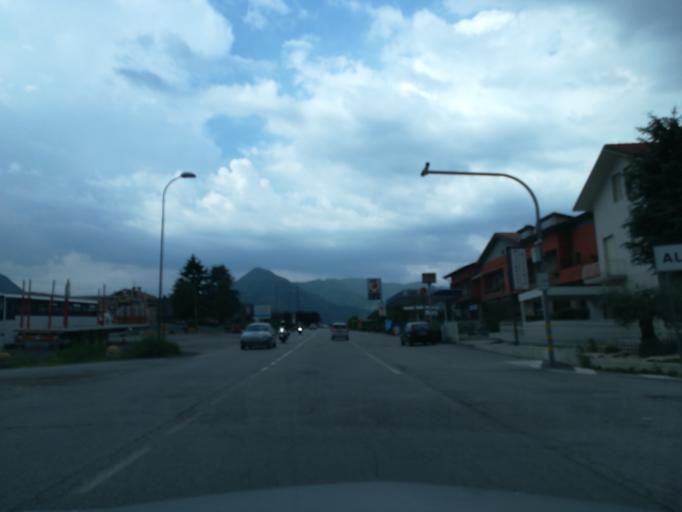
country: IT
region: Lombardy
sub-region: Provincia di Bergamo
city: Paladina
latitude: 45.7350
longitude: 9.6089
